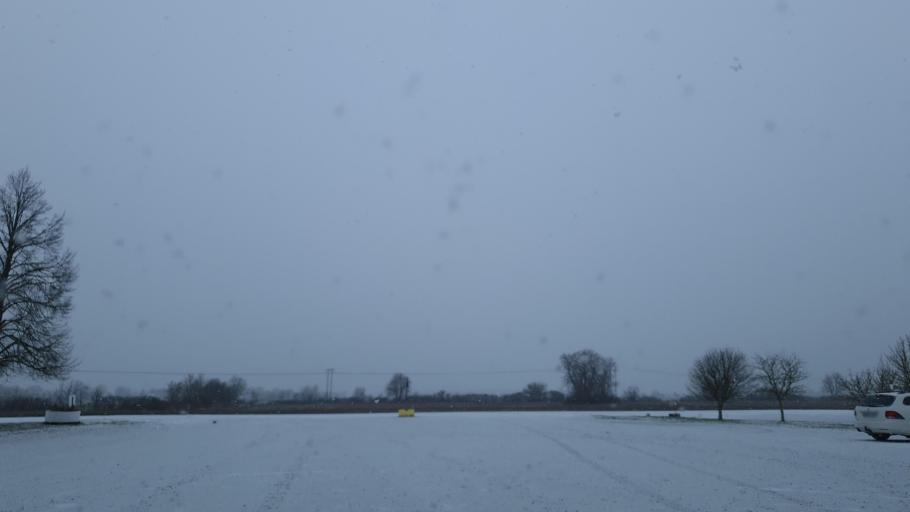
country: SE
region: Gotland
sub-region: Gotland
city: Visby
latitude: 57.5335
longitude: 18.4378
